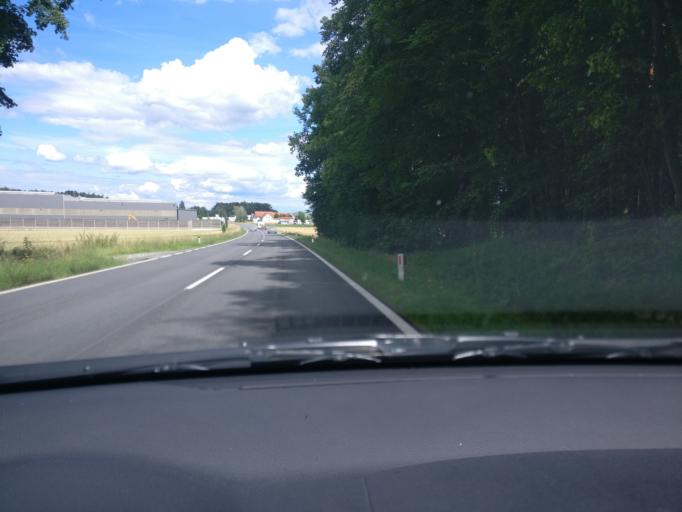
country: AT
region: Styria
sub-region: Politischer Bezirk Hartberg-Fuerstenfeld
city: Dienersdorf
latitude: 47.2133
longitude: 15.8701
